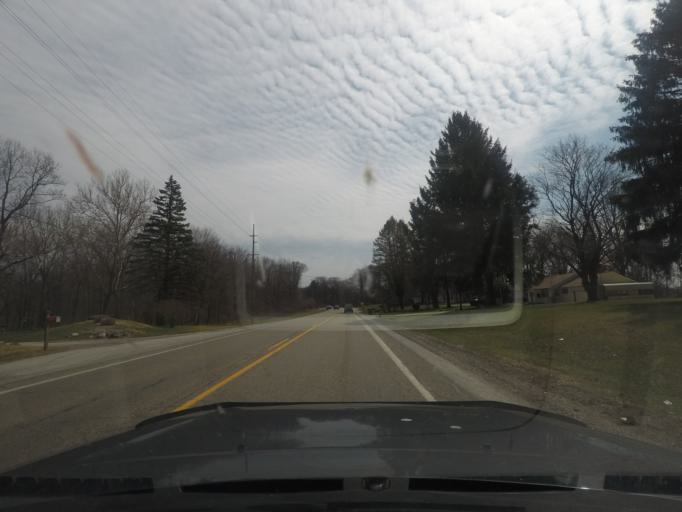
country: US
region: Indiana
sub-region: LaPorte County
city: LaPorte
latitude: 41.6535
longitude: -86.7623
